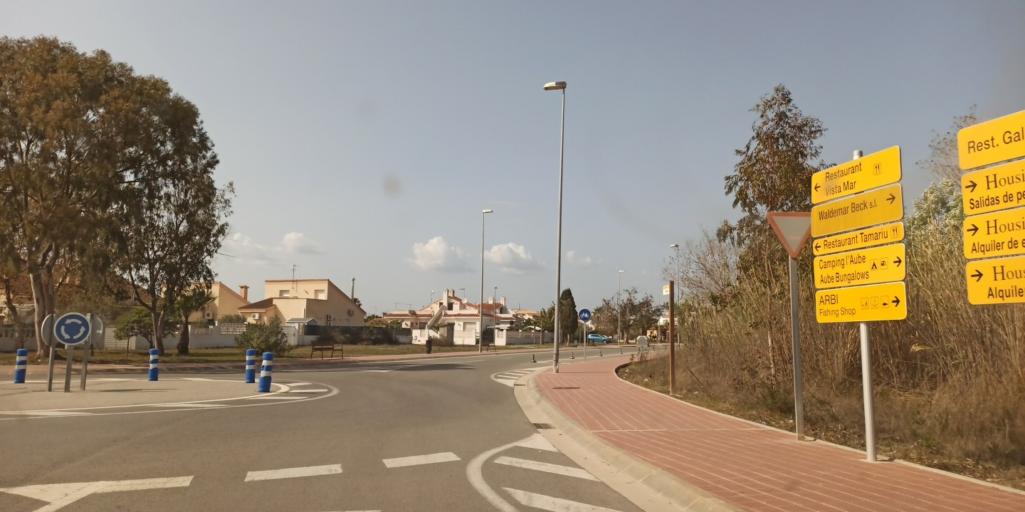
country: ES
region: Catalonia
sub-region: Provincia de Tarragona
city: Deltebre
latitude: 40.7234
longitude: 0.8429
